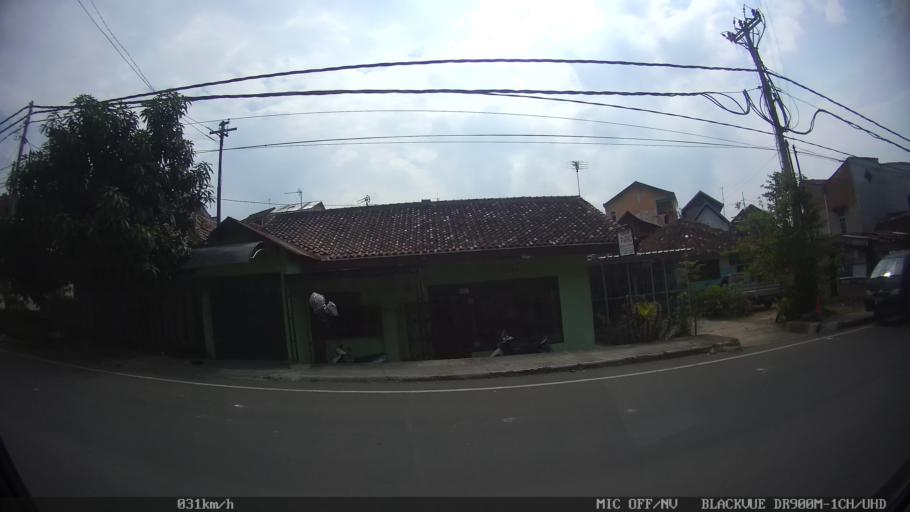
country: ID
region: Lampung
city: Bandarlampung
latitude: -5.4441
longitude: 105.2611
